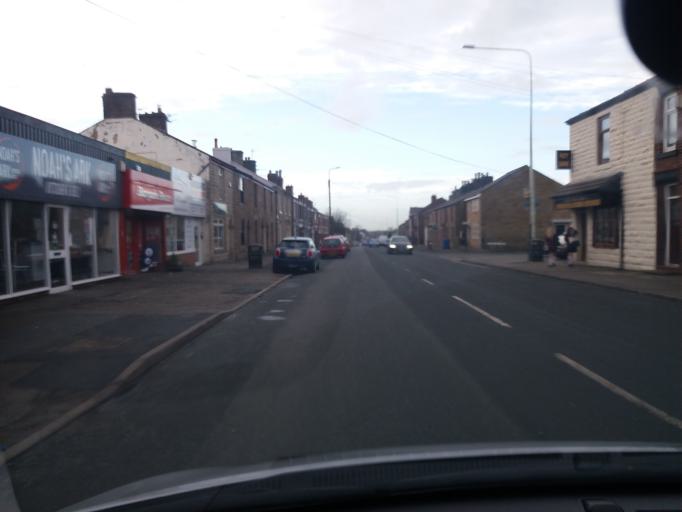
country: GB
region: England
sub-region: Lancashire
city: Adlington
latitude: 53.6191
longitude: -2.6001
